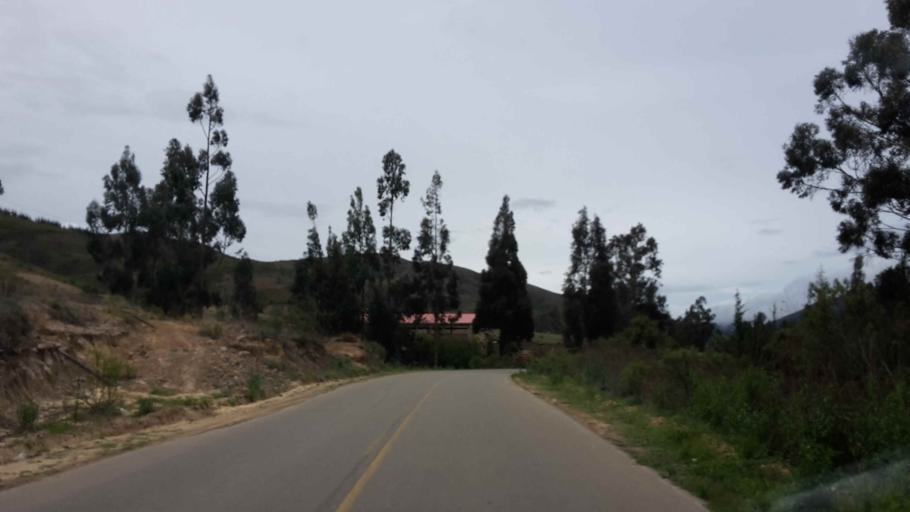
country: BO
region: Cochabamba
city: Totora
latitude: -17.6700
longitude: -65.2211
